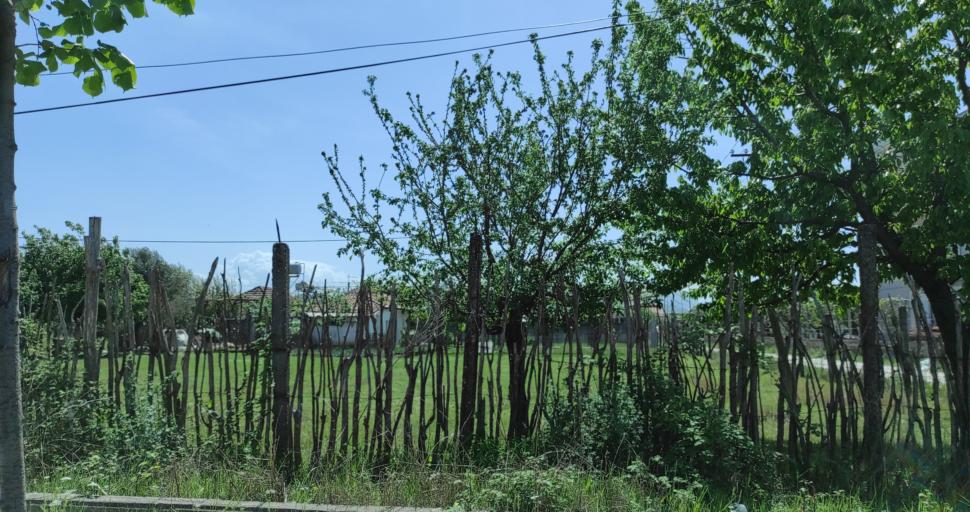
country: AL
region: Shkoder
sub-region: Rrethi i Shkodres
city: Shkoder
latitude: 42.1026
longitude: 19.5524
